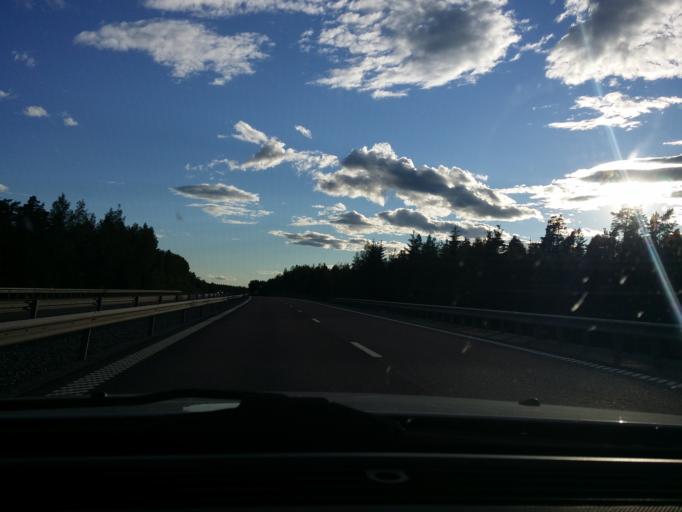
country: SE
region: Vaestmanland
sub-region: Vasteras
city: Tillberga
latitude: 59.6246
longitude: 16.7173
